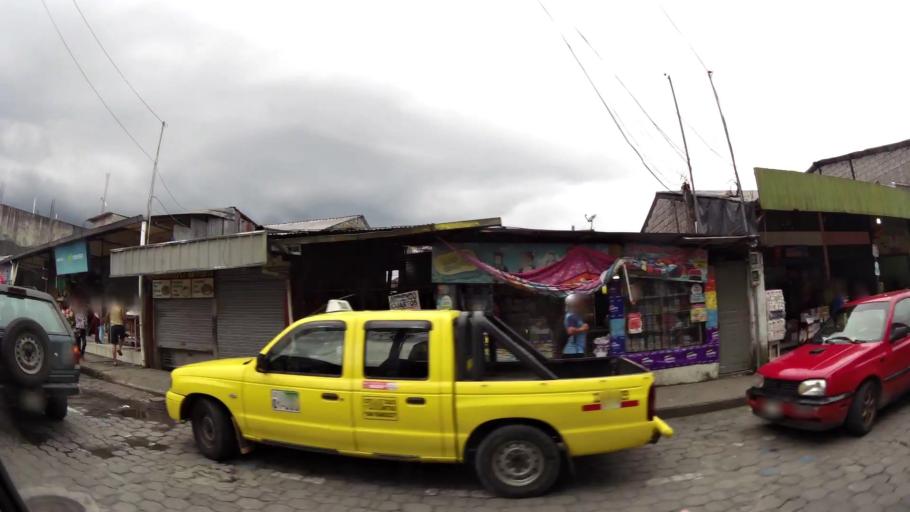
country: EC
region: Pastaza
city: Puyo
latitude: -1.4891
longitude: -77.9945
